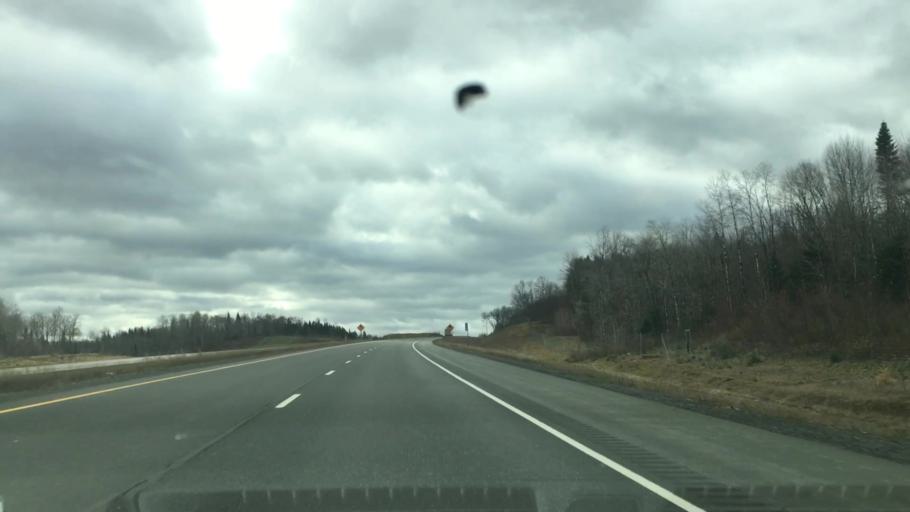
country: US
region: Maine
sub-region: Aroostook County
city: Fort Fairfield
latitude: 46.6635
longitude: -67.7311
